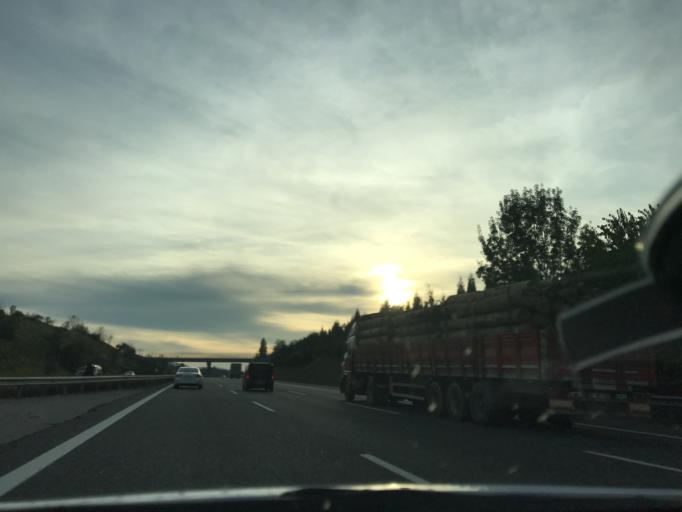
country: TR
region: Duzce
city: Gumusova
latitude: 40.8194
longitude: 30.9149
